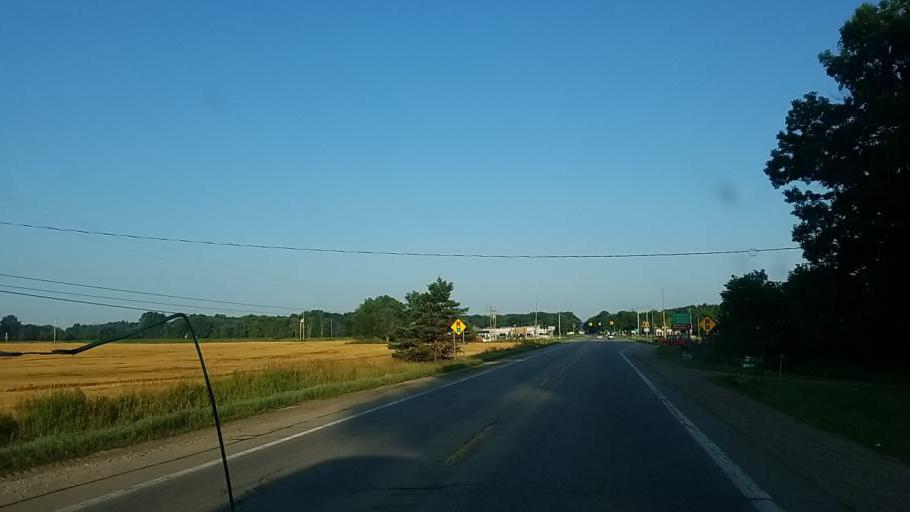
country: US
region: Michigan
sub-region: Montcalm County
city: Lakeview
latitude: 43.4315
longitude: -85.2597
